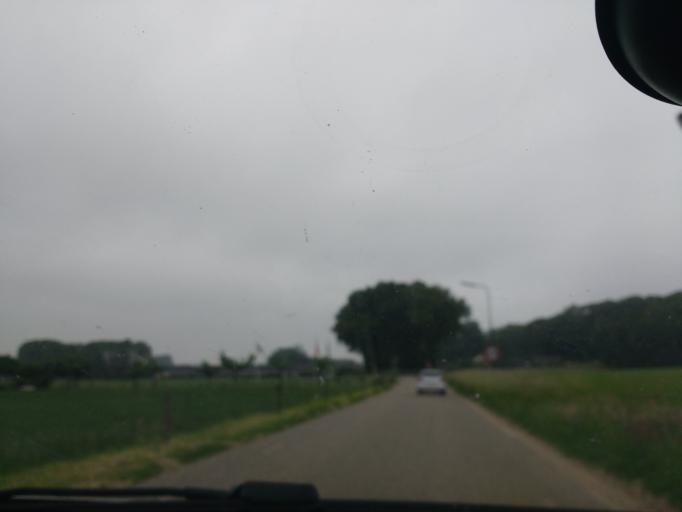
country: NL
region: Utrecht
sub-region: Gemeente Rhenen
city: Rhenen
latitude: 51.9611
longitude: 5.6034
